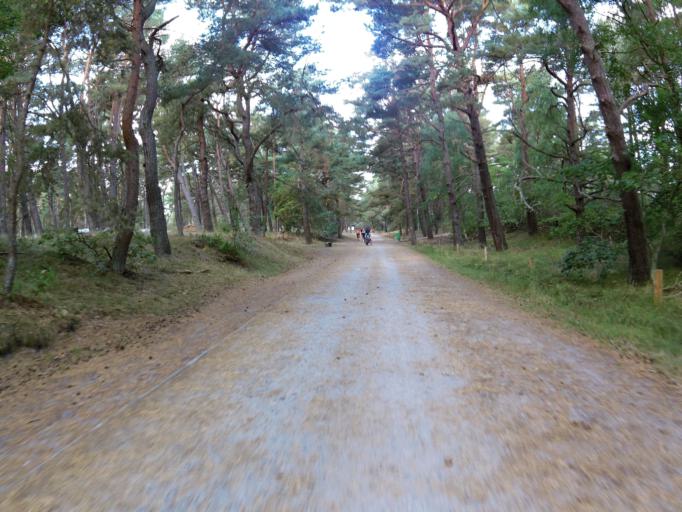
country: DE
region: Mecklenburg-Vorpommern
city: Ostseebad Zinnowitz
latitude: 54.0904
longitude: 13.8914
